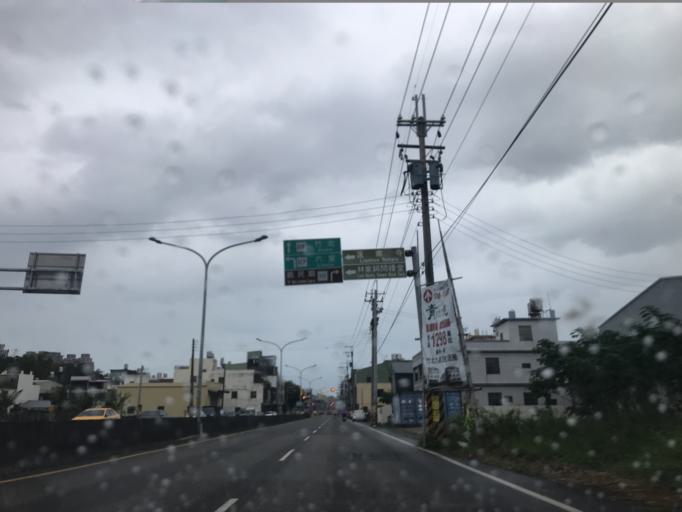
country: TW
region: Taiwan
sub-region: Hsinchu
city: Zhubei
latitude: 24.8303
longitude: 121.0398
